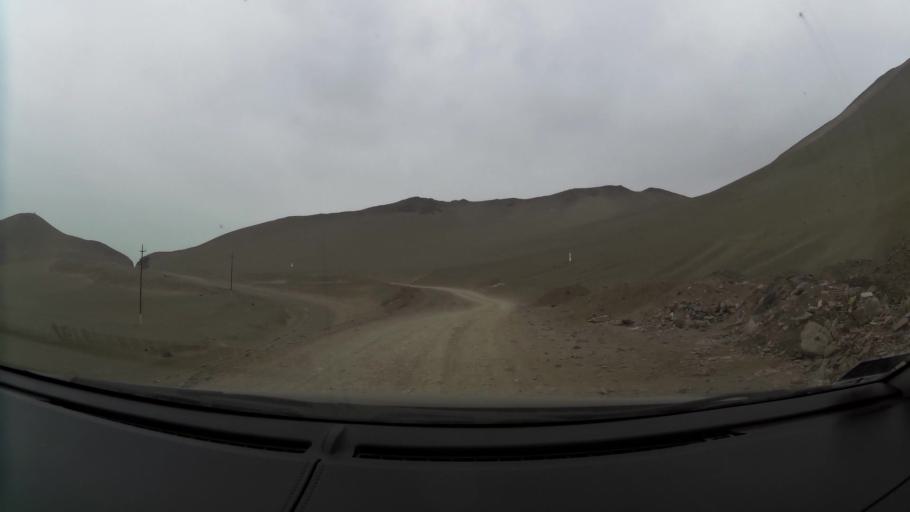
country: PE
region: Lima
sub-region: Lima
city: Santa Rosa
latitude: -11.8100
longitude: -77.1728
